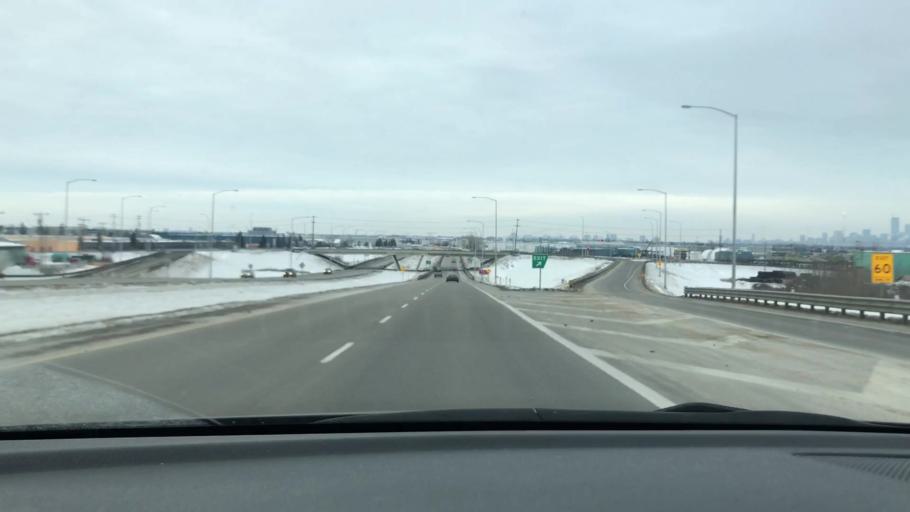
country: CA
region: Alberta
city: Sherwood Park
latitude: 53.5174
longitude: -113.3890
